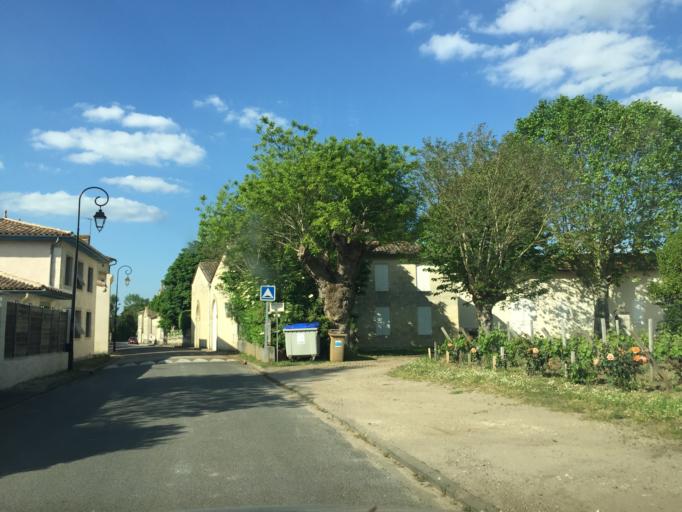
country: FR
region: Aquitaine
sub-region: Departement de la Gironde
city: Libourne
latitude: 44.9338
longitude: -0.2240
